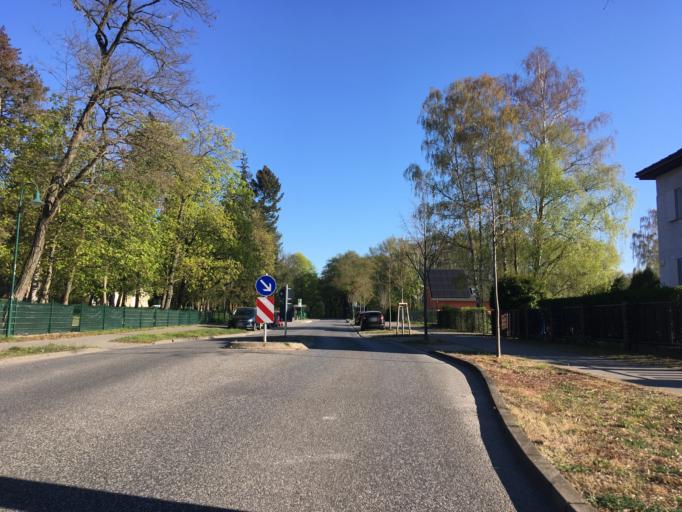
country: DE
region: Berlin
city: Buch
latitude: 52.6633
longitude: 13.5302
